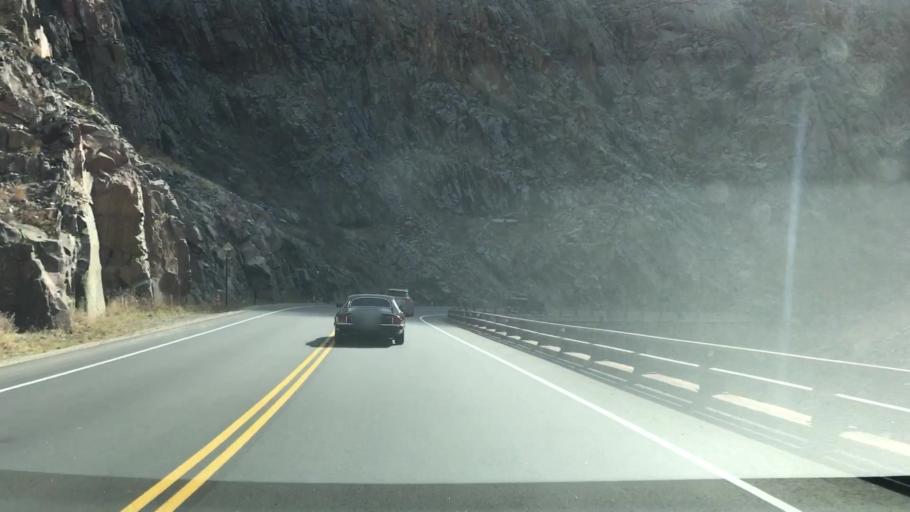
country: US
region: Colorado
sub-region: Larimer County
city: Loveland
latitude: 40.4224
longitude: -105.2382
